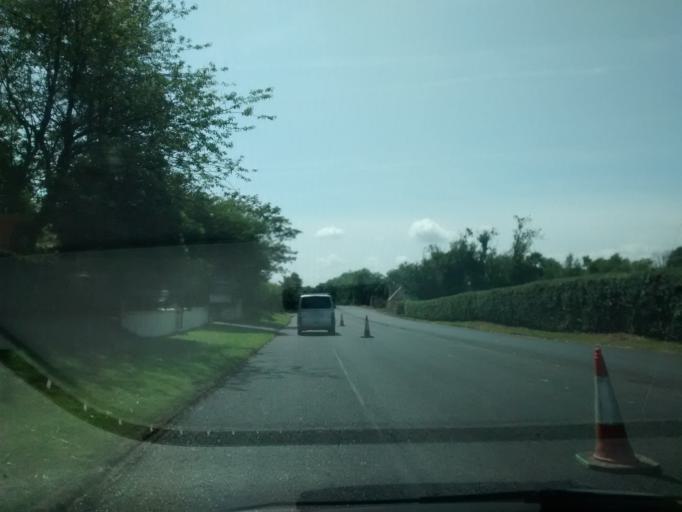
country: IE
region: Leinster
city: Lusk
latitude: 53.5149
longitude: -6.1915
